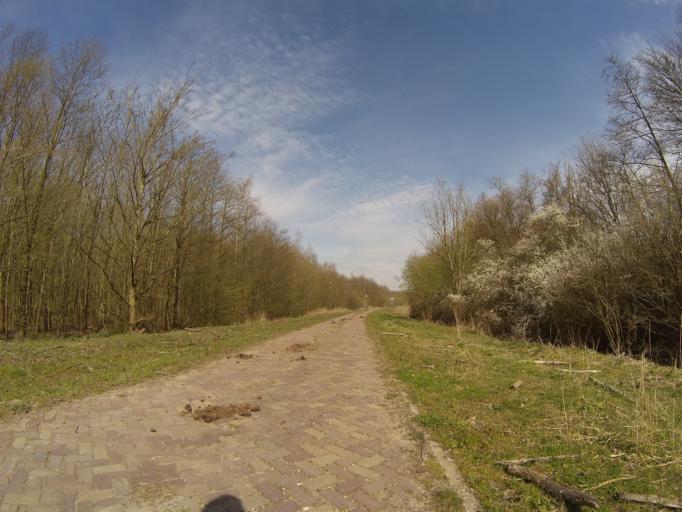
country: NL
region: Gelderland
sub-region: Gemeente Nijkerk
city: Nijkerk
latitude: 52.2863
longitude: 5.4798
